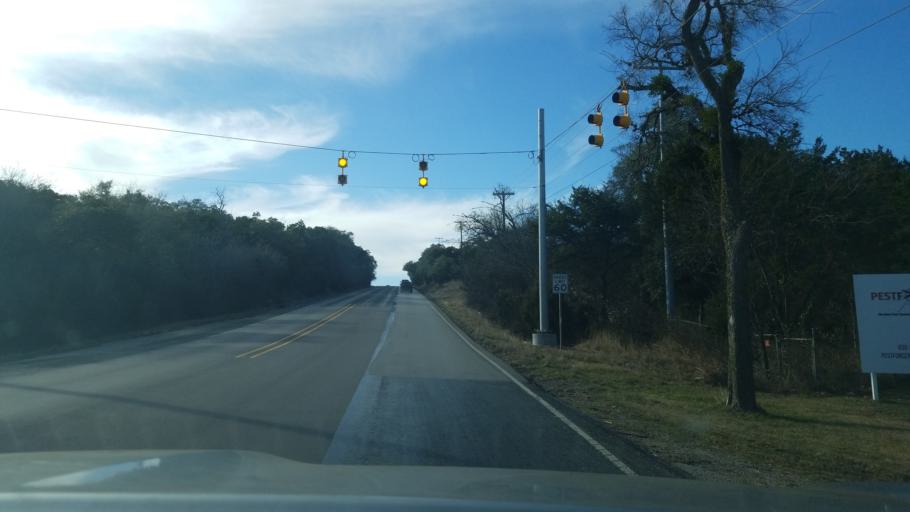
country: US
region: Texas
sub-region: Comal County
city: Canyon Lake
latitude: 29.7729
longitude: -98.2763
